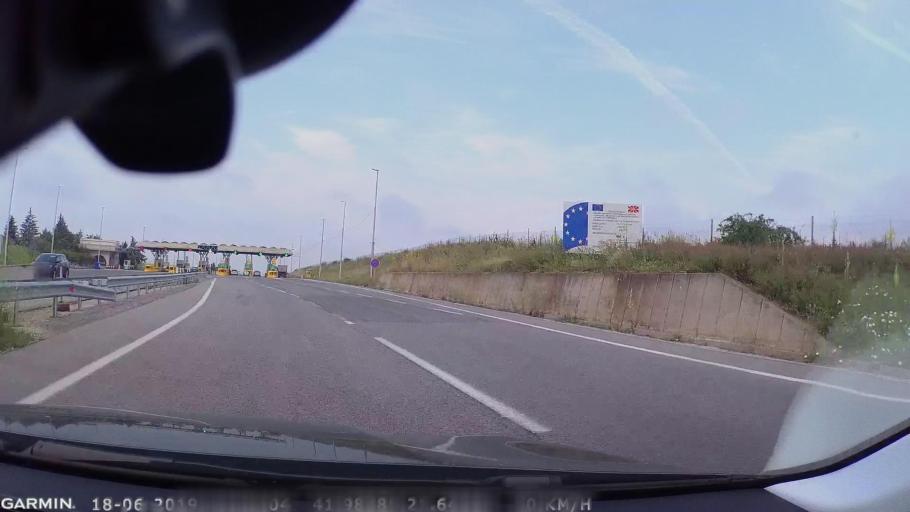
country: MK
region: Petrovec
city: Sredno Konjare
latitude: 41.9552
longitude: 21.7477
